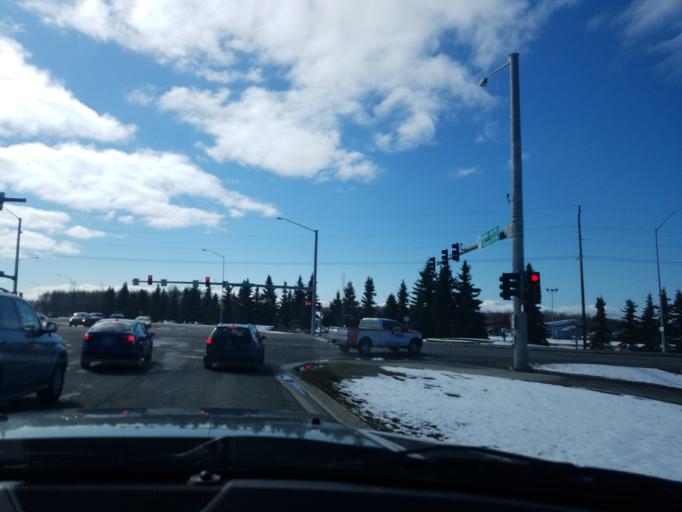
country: US
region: Alaska
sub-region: Anchorage Municipality
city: Anchorage
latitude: 61.1742
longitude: -149.9439
